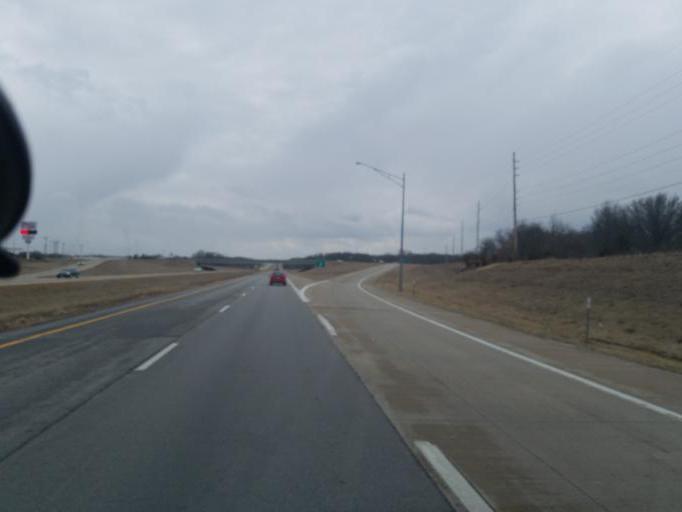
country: US
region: Missouri
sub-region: Randolph County
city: Moberly
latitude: 39.3974
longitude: -92.4130
